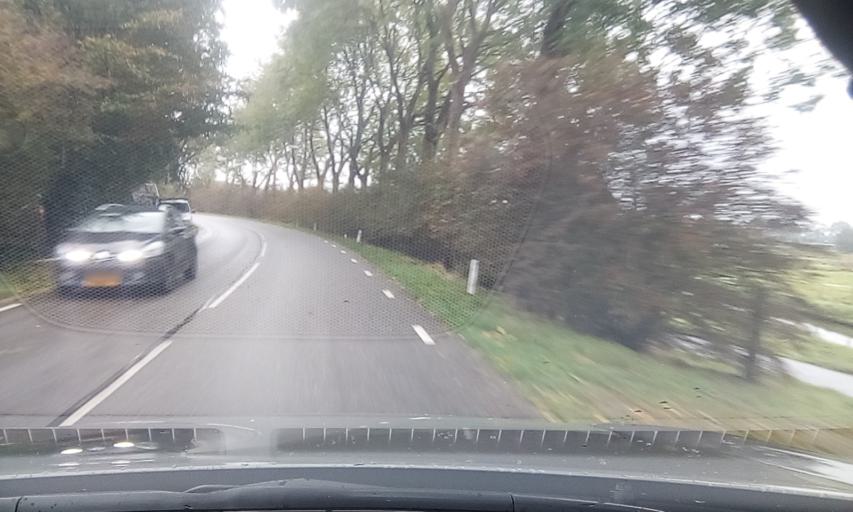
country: NL
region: Groningen
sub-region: Gemeente Haren
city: Haren
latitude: 53.2131
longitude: 6.6537
